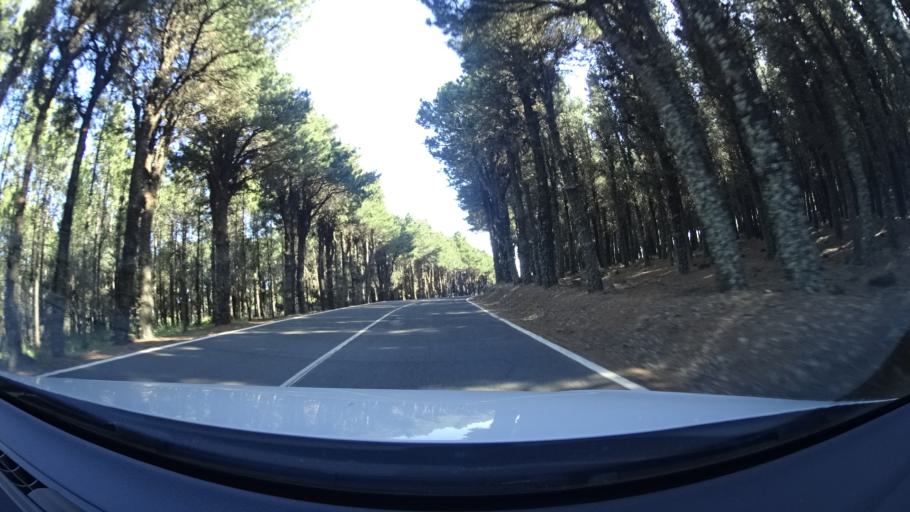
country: ES
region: Canary Islands
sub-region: Provincia de Las Palmas
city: Vega de San Mateo
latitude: 27.9655
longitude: -15.5466
